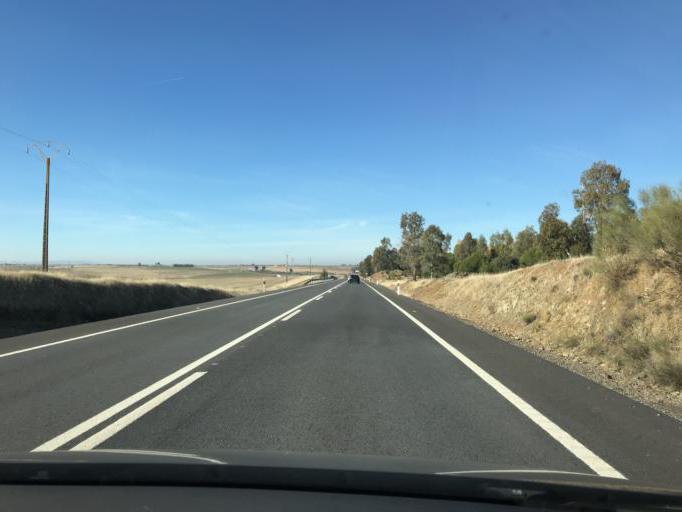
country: ES
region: Extremadura
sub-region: Provincia de Badajoz
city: Granja de Torrehermosa
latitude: 38.3001
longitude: -5.5951
